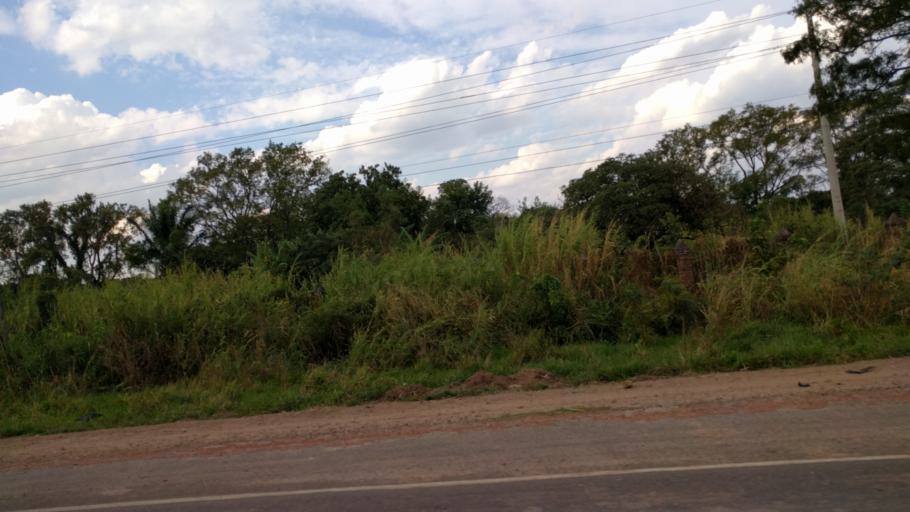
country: BO
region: Santa Cruz
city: Warnes
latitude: -17.4378
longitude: -63.1922
